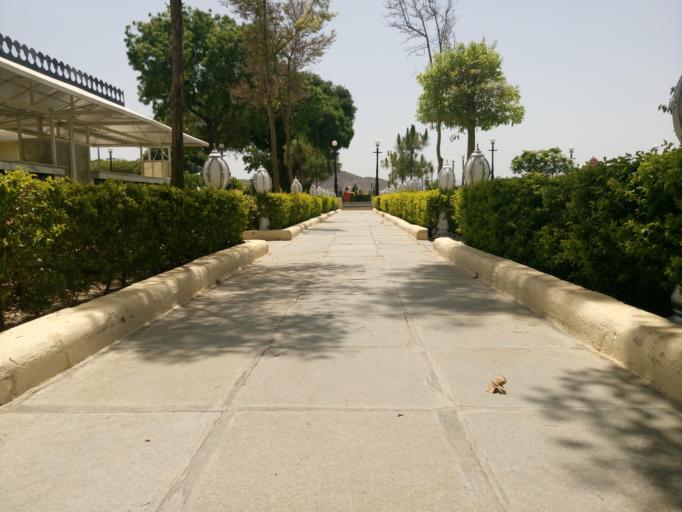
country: IN
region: Rajasthan
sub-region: Udaipur
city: Udaipur
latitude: 24.5680
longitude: 73.6780
